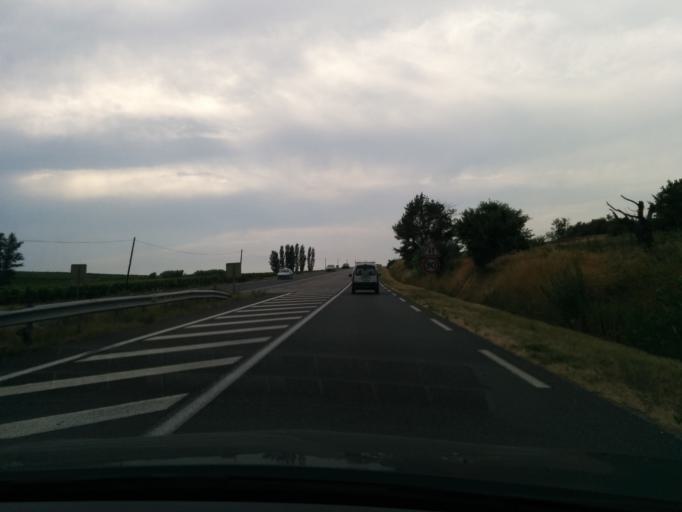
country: FR
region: Languedoc-Roussillon
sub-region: Departement de l'Aude
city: Pezens
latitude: 43.2476
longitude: 2.2882
